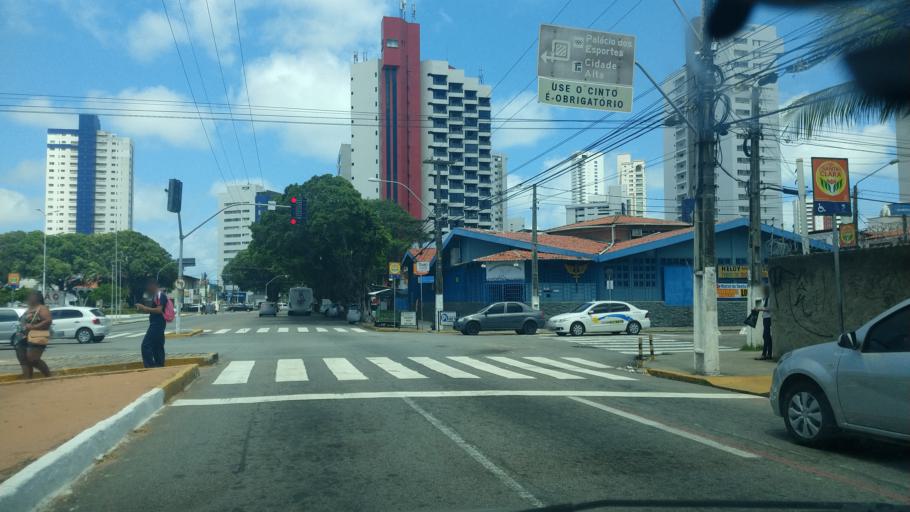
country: BR
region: Rio Grande do Norte
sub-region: Natal
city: Natal
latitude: -5.7852
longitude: -35.2003
